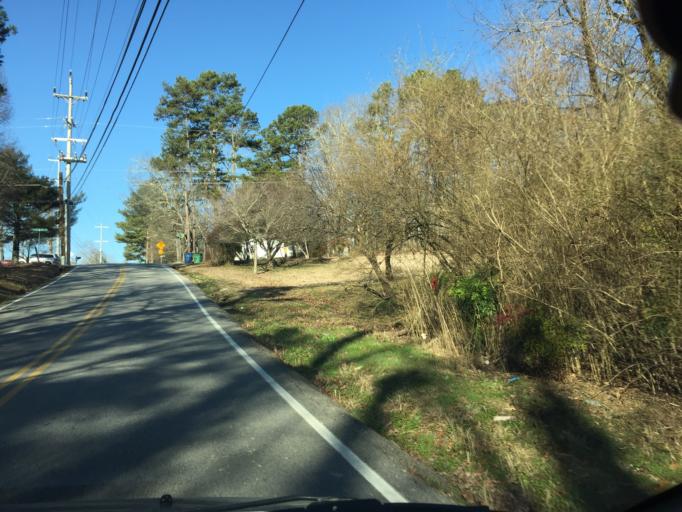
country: US
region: Tennessee
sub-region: Hamilton County
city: Collegedale
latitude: 35.0389
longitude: -85.0921
